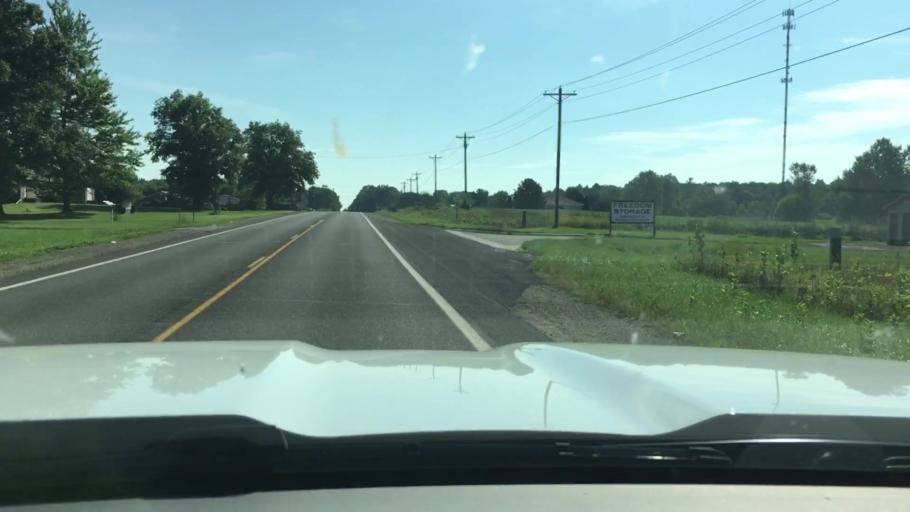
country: US
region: Michigan
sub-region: Montcalm County
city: Edmore
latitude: 43.4083
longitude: -84.9126
